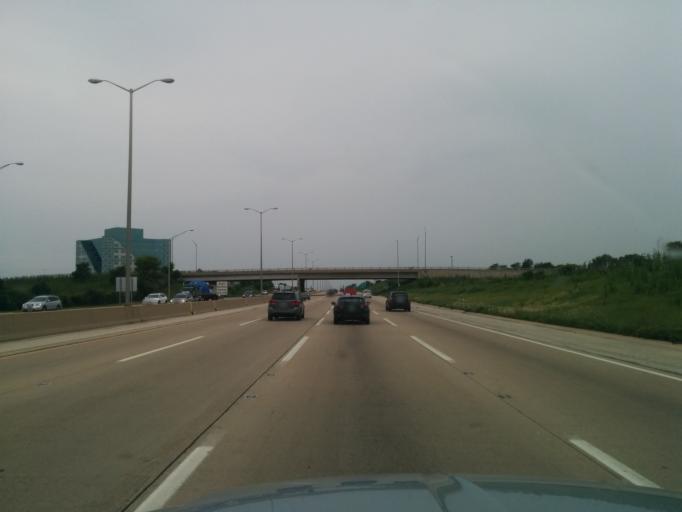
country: US
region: Illinois
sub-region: DuPage County
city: Naperville
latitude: 41.8064
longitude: -88.1391
